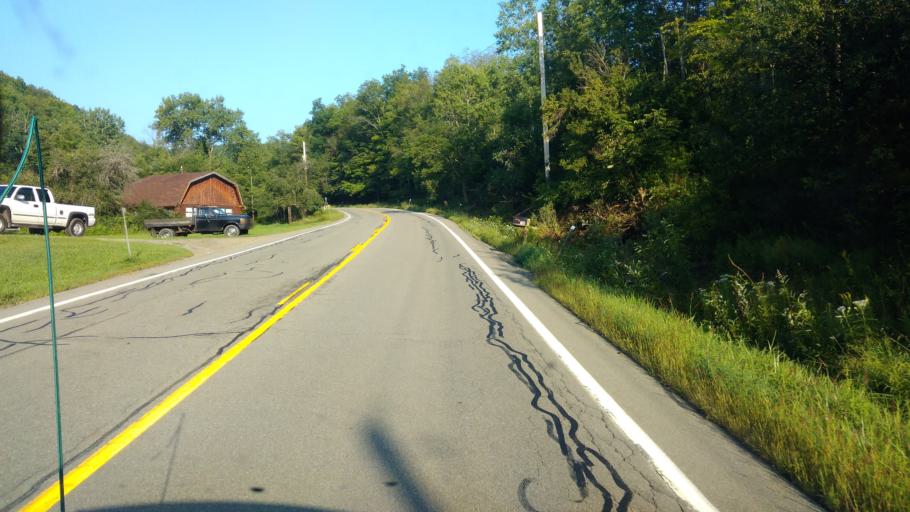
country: US
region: New York
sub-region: Allegany County
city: Andover
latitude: 42.1420
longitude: -77.6721
